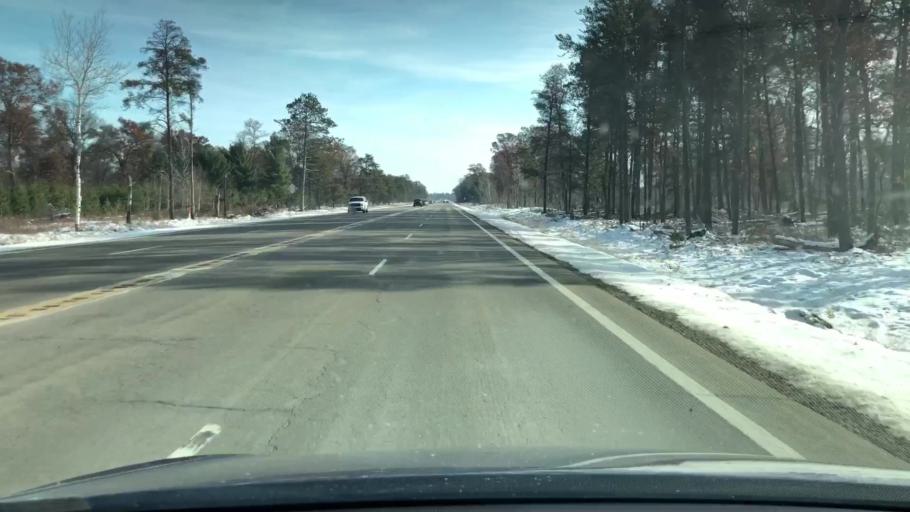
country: US
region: Michigan
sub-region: Crawford County
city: Grayling
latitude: 44.6607
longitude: -84.7606
